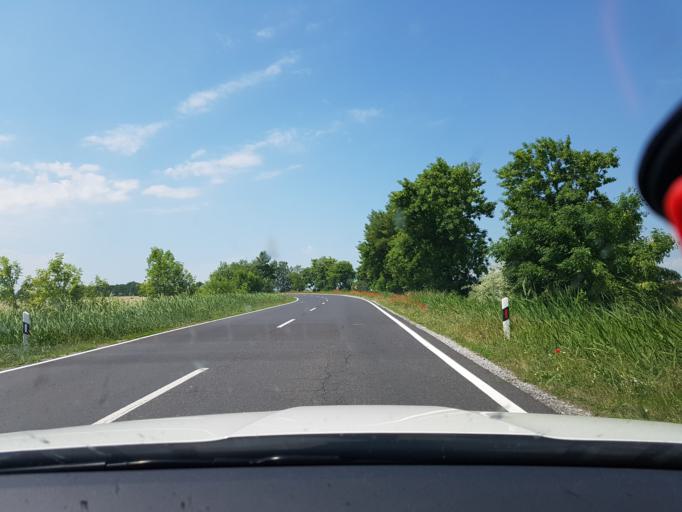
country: HU
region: Hajdu-Bihar
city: Egyek
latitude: 47.5507
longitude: 20.9479
